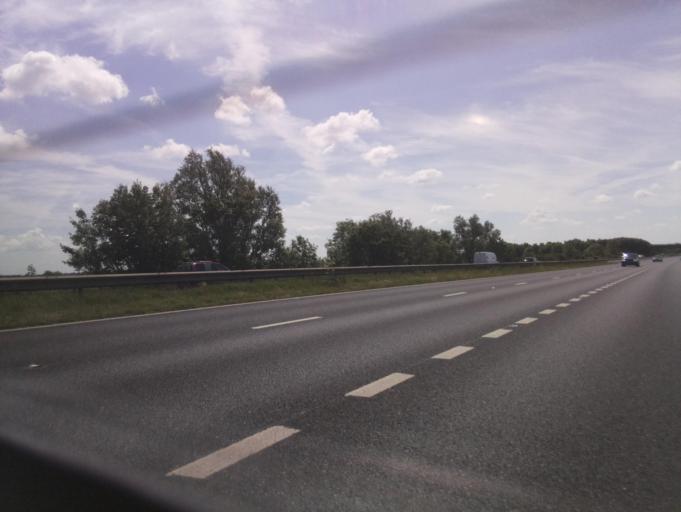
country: GB
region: England
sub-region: East Riding of Yorkshire
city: Rawcliffe
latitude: 53.6733
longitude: -0.9646
